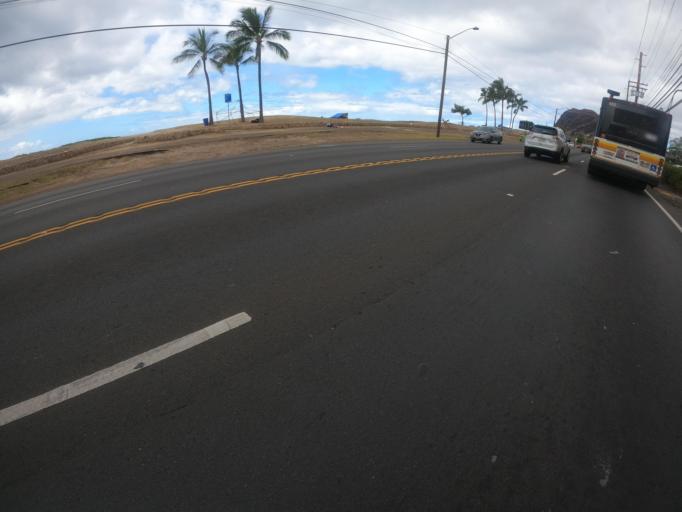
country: US
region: Hawaii
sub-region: Honolulu County
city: Nanakuli
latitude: 21.3868
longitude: -158.1512
